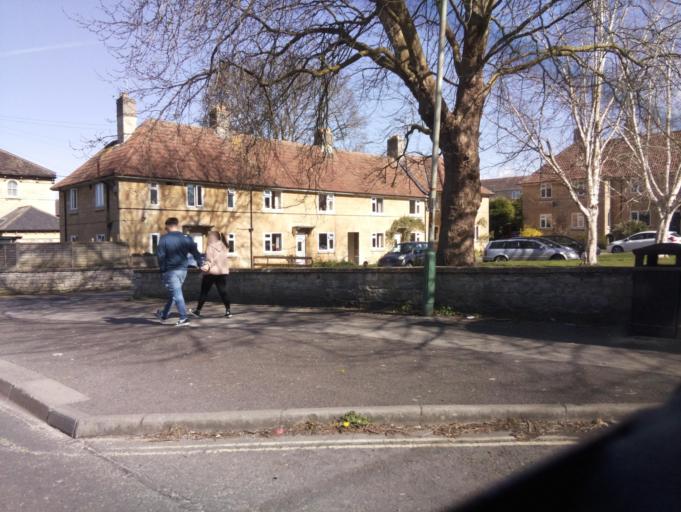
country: GB
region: England
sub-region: Wiltshire
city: Bradford-on-Avon
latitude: 51.3414
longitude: -2.2461
